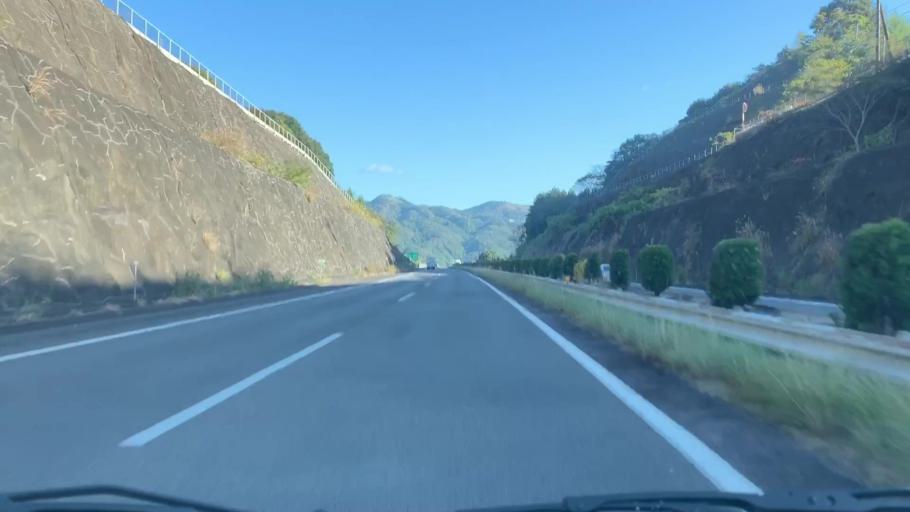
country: JP
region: Saga Prefecture
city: Takeocho-takeo
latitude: 33.2789
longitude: 130.1180
